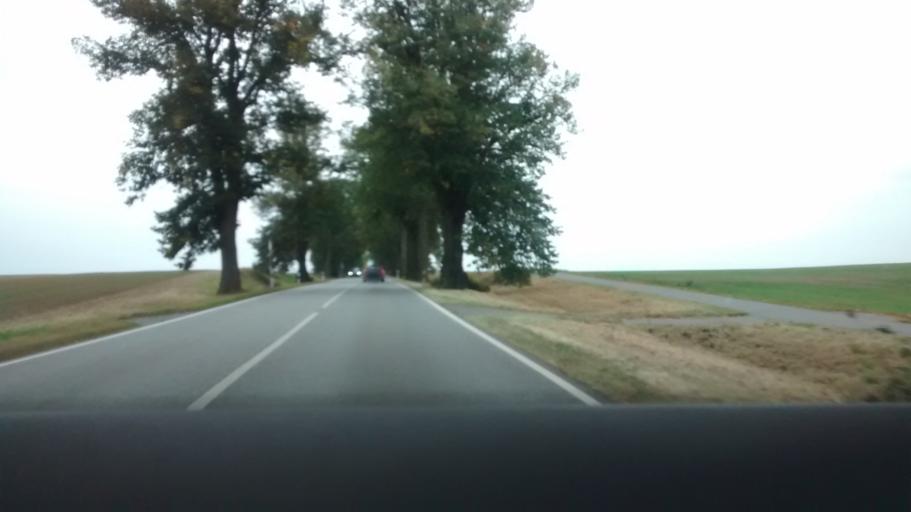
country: DE
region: Mecklenburg-Vorpommern
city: Mecklenburg
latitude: 53.8354
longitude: 11.4570
